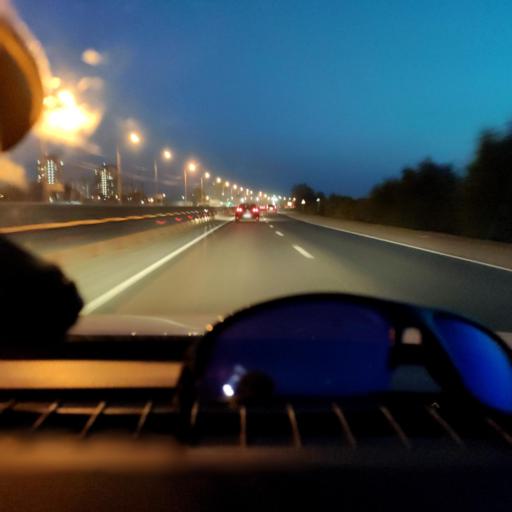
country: RU
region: Samara
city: Samara
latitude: 53.1000
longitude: 50.1604
